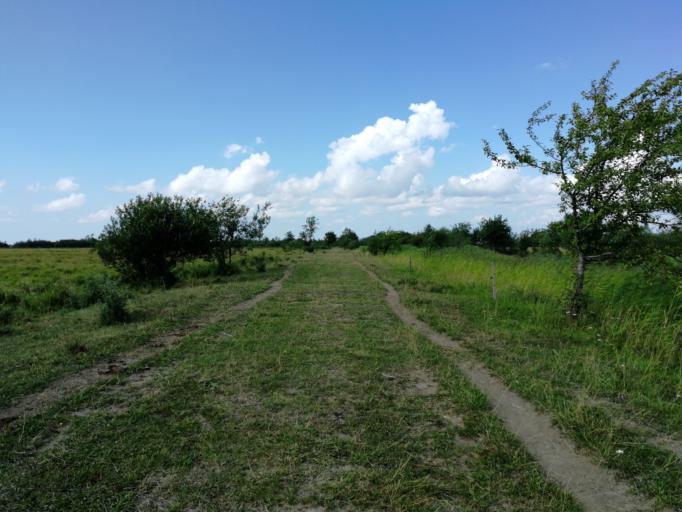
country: EE
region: Laeaene
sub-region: Lihula vald
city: Lihula
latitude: 58.7216
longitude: 23.8086
